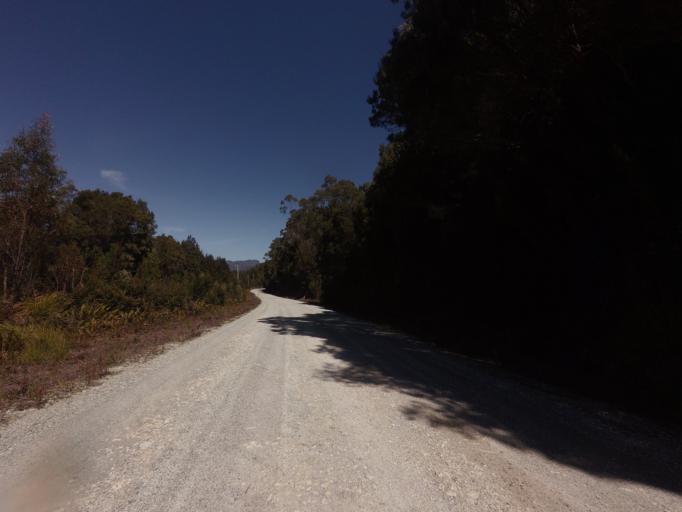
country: AU
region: Tasmania
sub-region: West Coast
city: Queenstown
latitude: -42.7592
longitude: 145.9852
